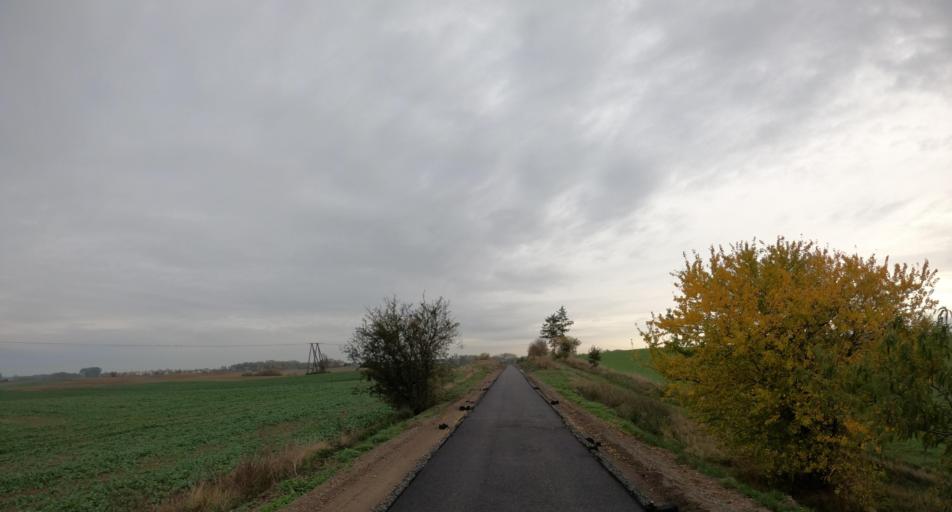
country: PL
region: West Pomeranian Voivodeship
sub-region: Powiat mysliborski
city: Nowogrodek Pomorski
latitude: 52.9837
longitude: 15.0497
